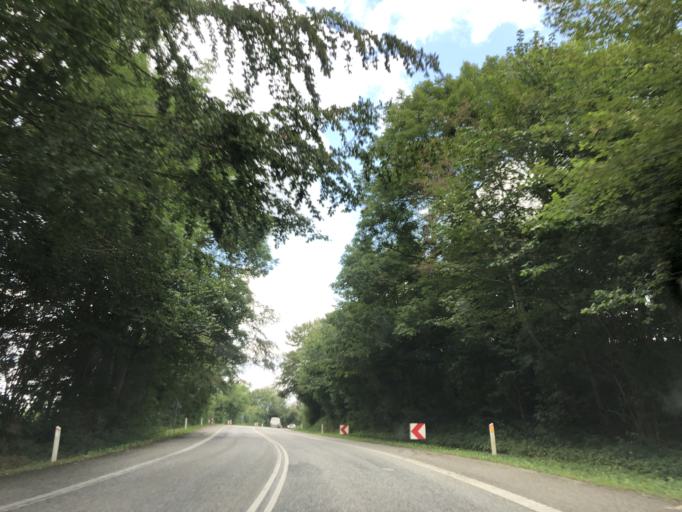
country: DK
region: South Denmark
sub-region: Aabenraa Kommune
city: Lojt Kirkeby
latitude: 55.1259
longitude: 9.4414
